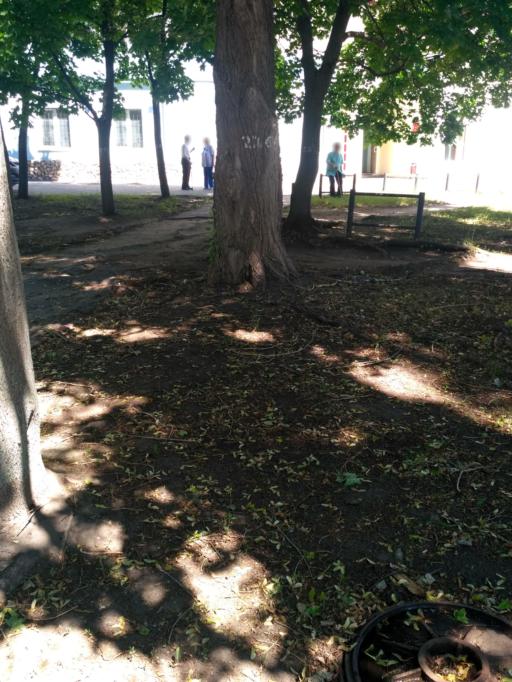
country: RU
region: Voronezj
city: Voronezh
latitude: 51.6454
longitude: 39.1495
